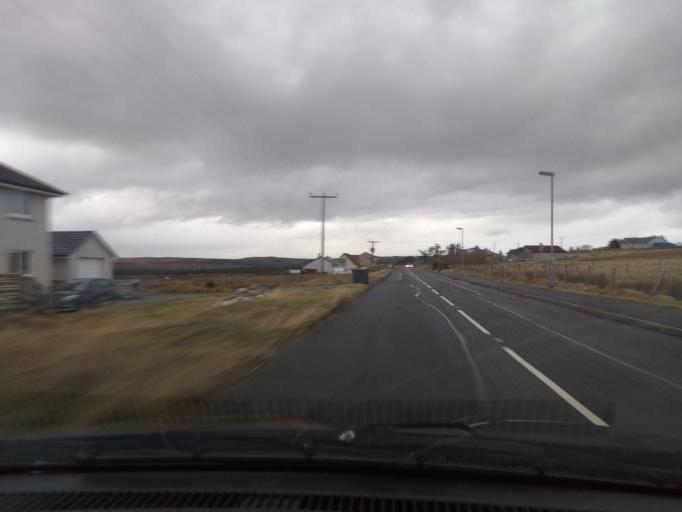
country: GB
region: Scotland
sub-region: Eilean Siar
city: Isle of Lewis
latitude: 58.2412
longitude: -6.3524
